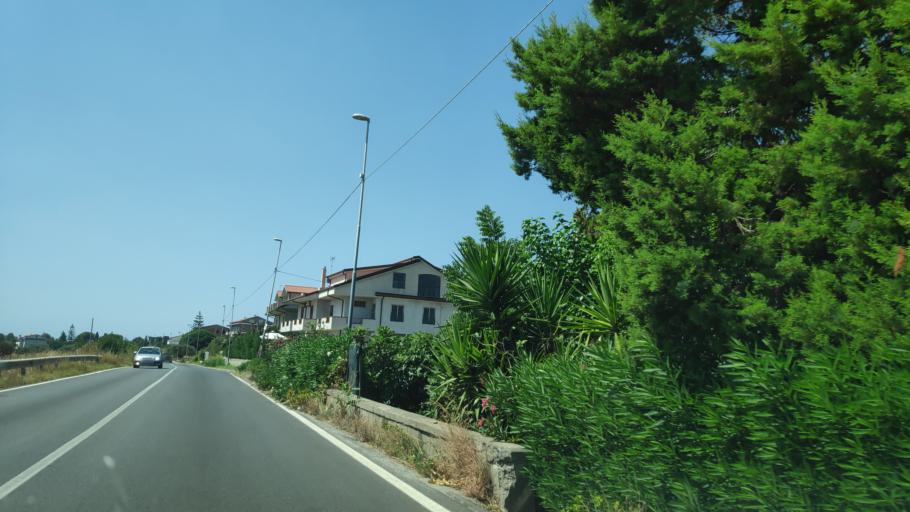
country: IT
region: Calabria
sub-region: Provincia di Reggio Calabria
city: Weather Station
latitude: 37.9528
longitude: 16.0903
